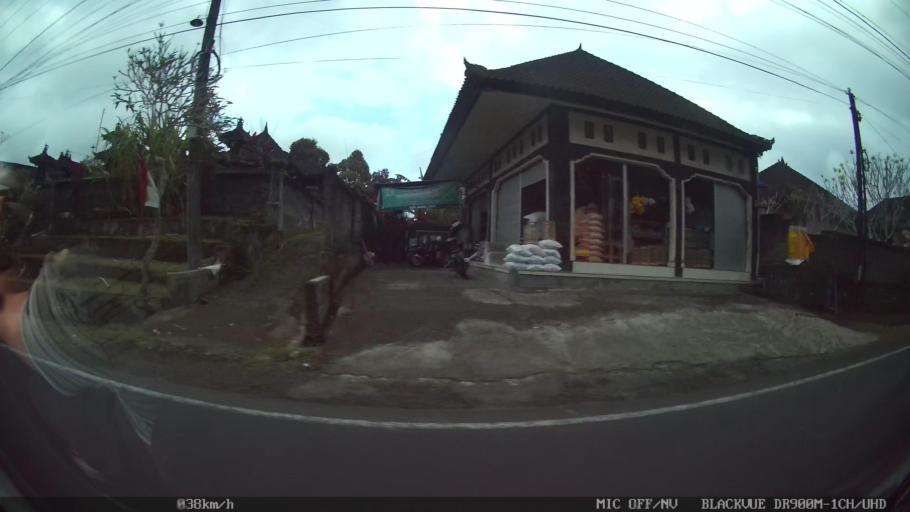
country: ID
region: Bali
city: Penebel
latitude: -8.4163
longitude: 115.1447
